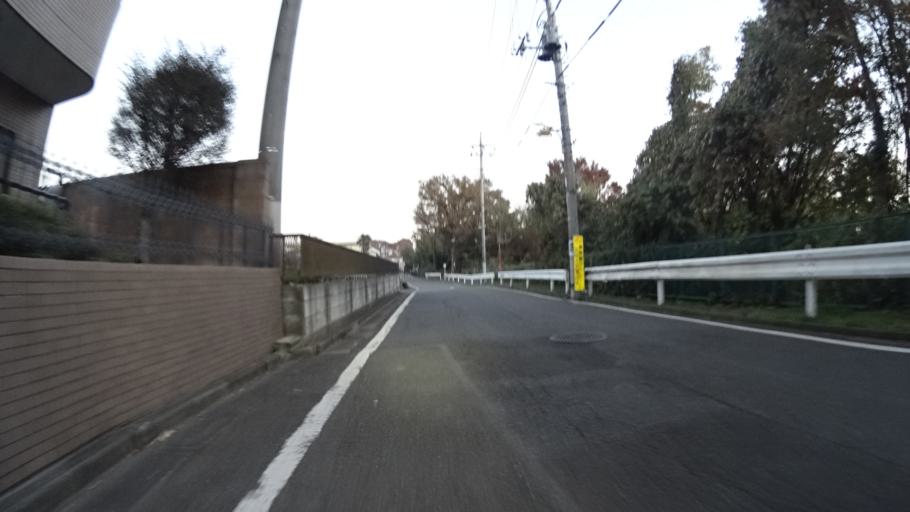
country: JP
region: Tokyo
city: Hino
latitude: 35.6821
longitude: 139.4206
